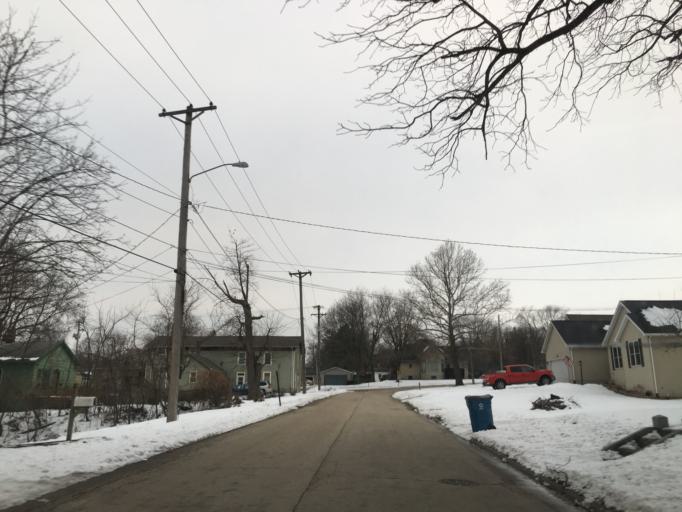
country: US
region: Illinois
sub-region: LaSalle County
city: Peru
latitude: 41.3255
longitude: -89.1239
